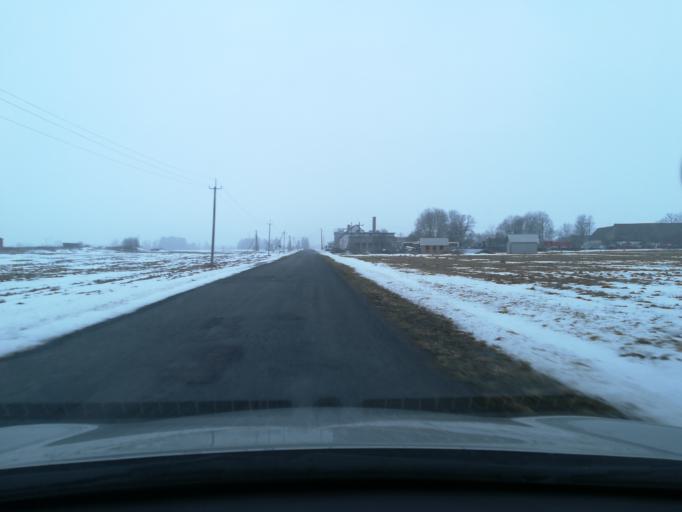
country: EE
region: Harju
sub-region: Raasiku vald
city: Raasiku
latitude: 59.3553
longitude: 25.2056
